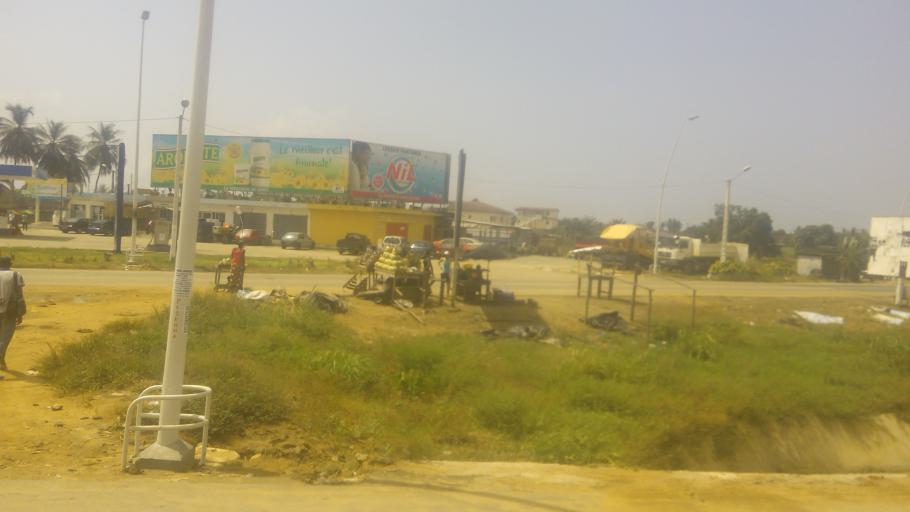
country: CI
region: Sud-Comoe
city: Grand-Bassam
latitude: 5.2226
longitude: -3.7257
